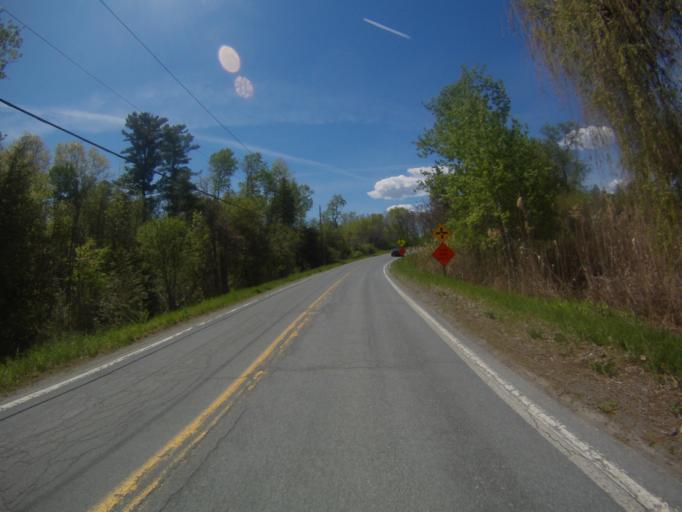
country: US
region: New York
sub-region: Essex County
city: Port Henry
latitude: 43.9642
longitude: -73.4208
